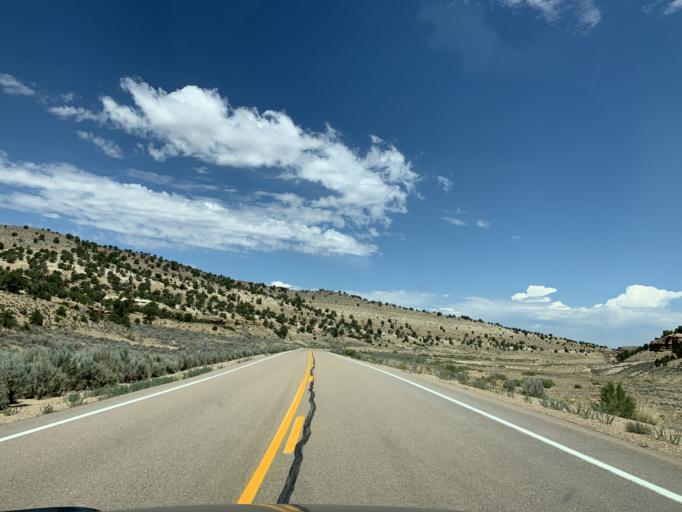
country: US
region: Utah
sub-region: Duchesne County
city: Duchesne
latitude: 39.9828
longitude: -110.1620
